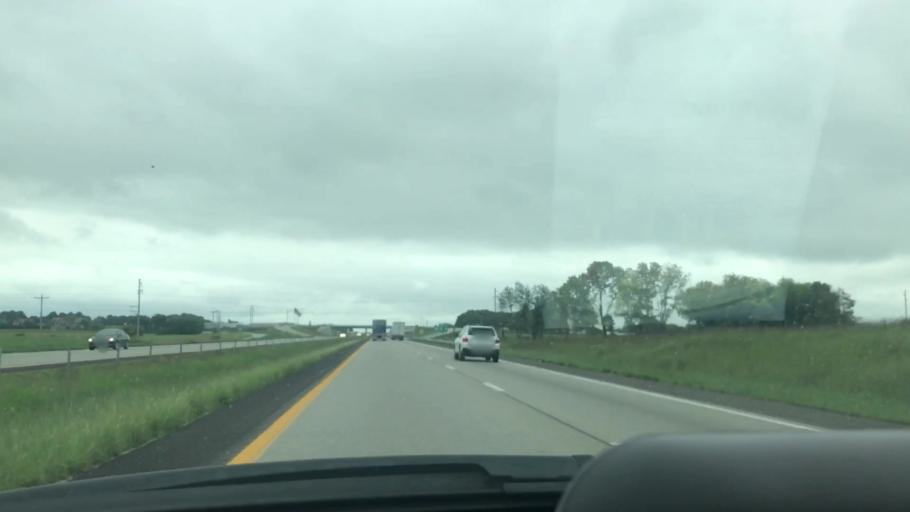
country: US
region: Missouri
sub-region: Greene County
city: Republic
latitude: 37.1991
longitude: -93.4296
